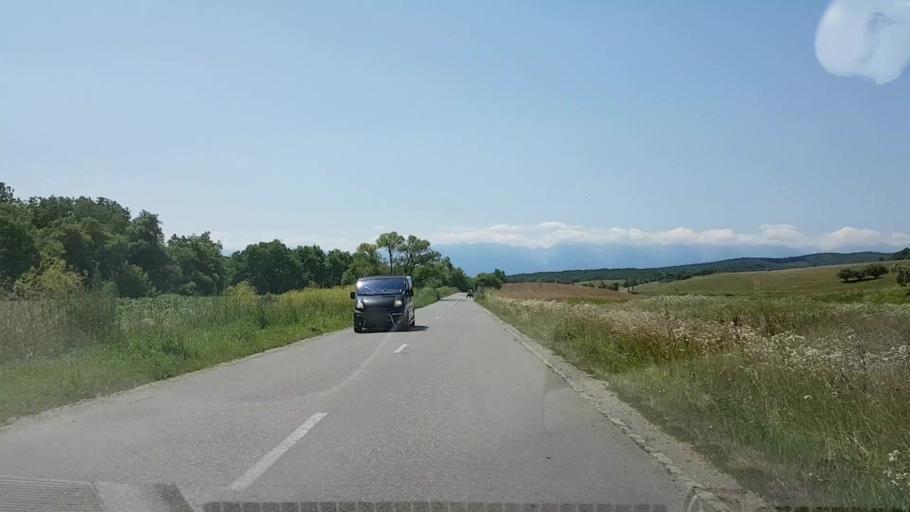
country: RO
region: Brasov
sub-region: Comuna Cincu
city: Cincu
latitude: 45.9008
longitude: 24.8119
